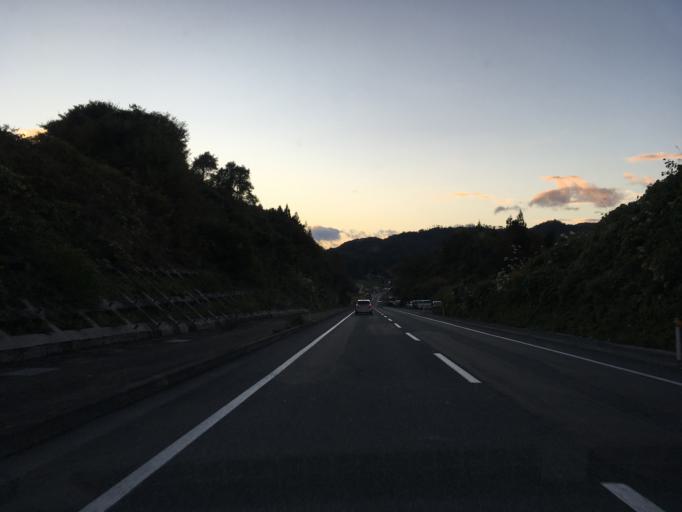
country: JP
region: Iwate
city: Kitakami
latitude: 39.2895
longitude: 141.2694
